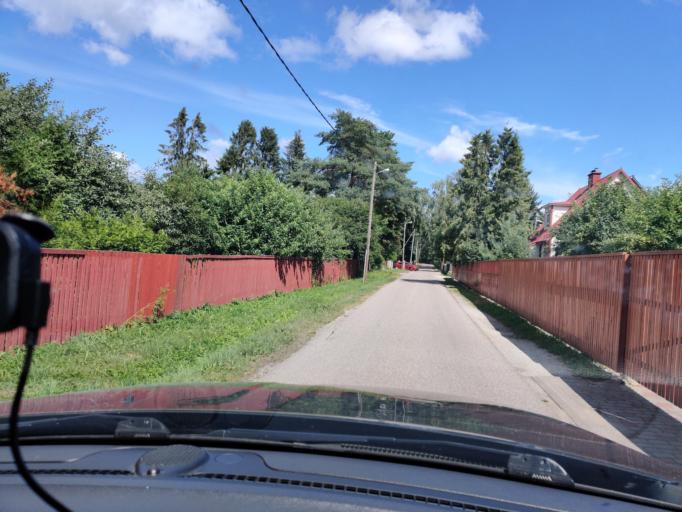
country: EE
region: Harju
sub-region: Saue vald
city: Laagri
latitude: 59.3752
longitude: 24.6383
